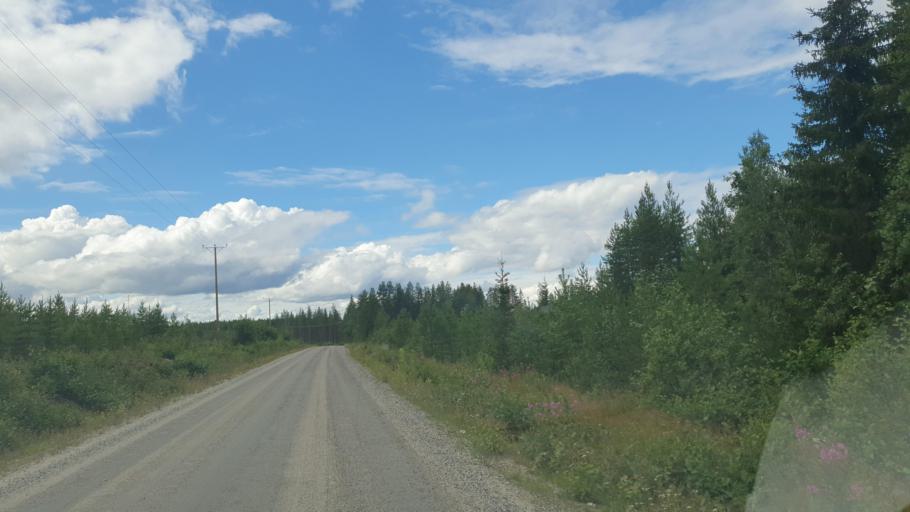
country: FI
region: Kainuu
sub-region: Kehys-Kainuu
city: Kuhmo
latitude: 64.1107
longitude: 29.3685
